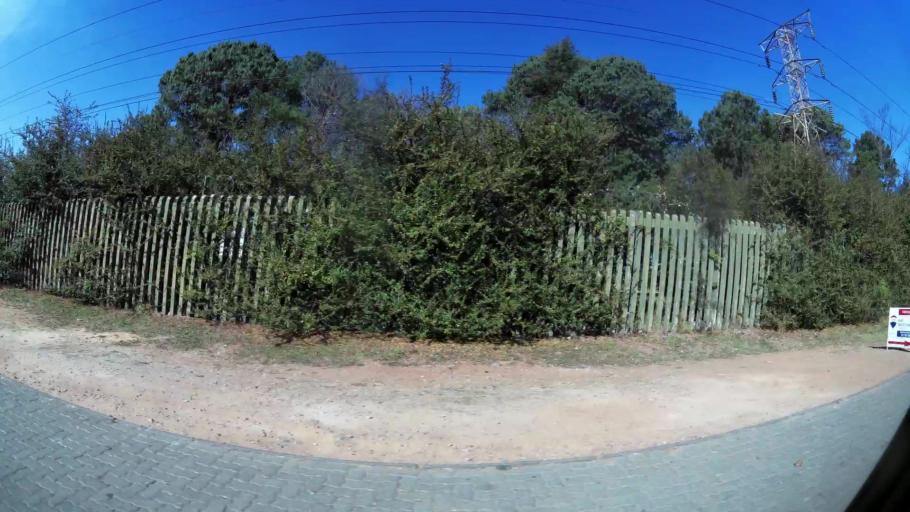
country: ZA
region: Gauteng
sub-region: City of Johannesburg Metropolitan Municipality
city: Roodepoort
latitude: -26.1005
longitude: 27.9649
